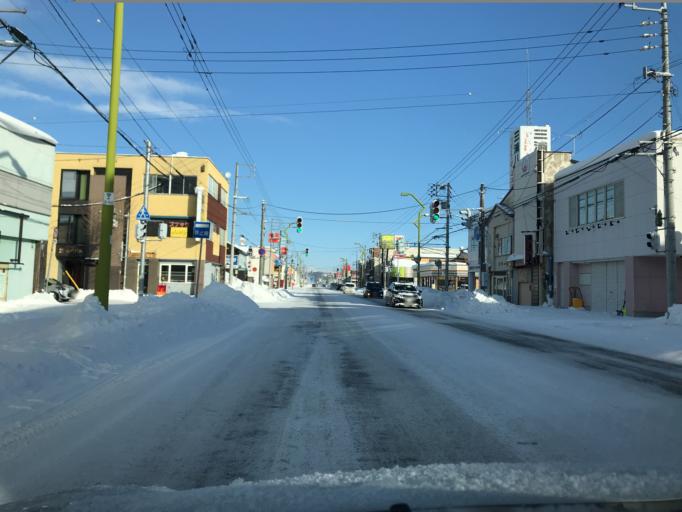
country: JP
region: Hokkaido
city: Nayoro
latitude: 44.3511
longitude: 142.4571
